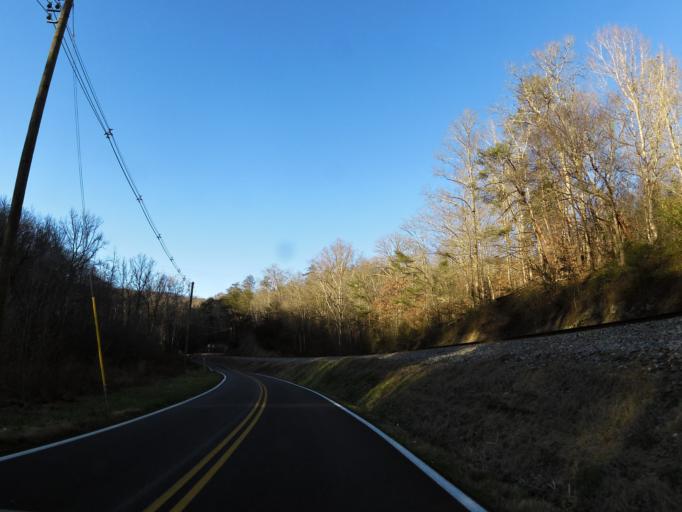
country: US
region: Tennessee
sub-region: Anderson County
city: Oak Ridge
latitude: 36.0713
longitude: -84.2468
